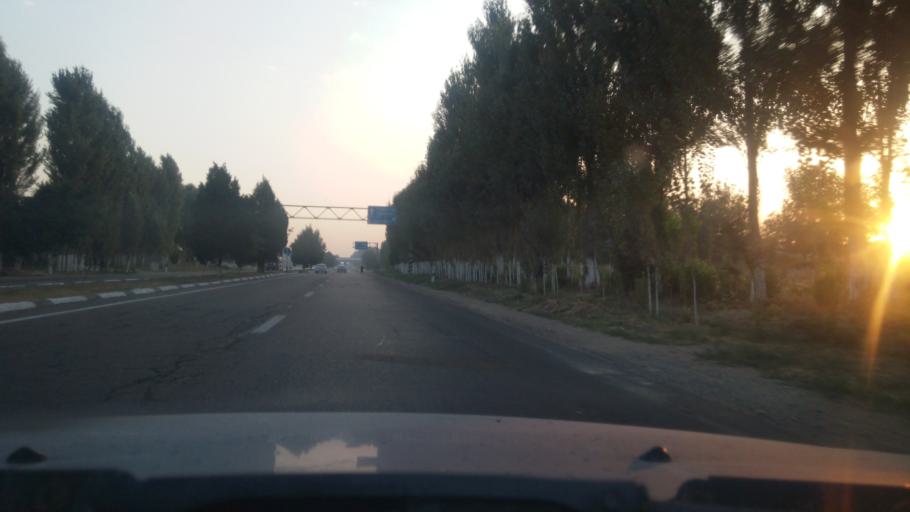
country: UZ
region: Toshkent
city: Amir Timur
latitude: 41.0807
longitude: 68.9385
